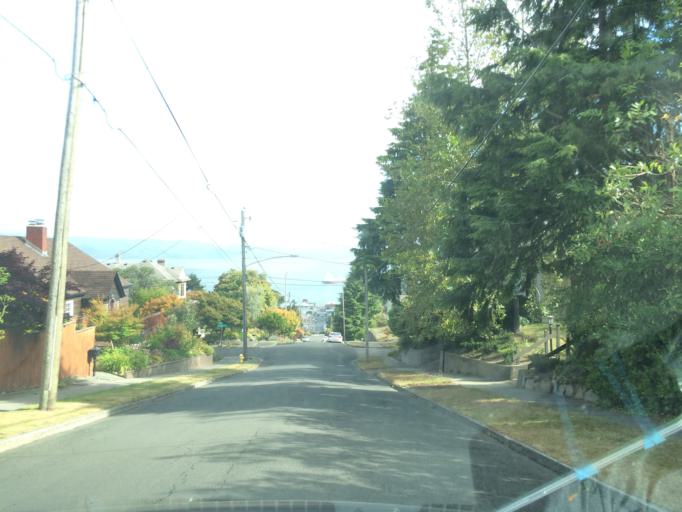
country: US
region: Oregon
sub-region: Clatsop County
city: Astoria
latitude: 46.1822
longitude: -123.8320
